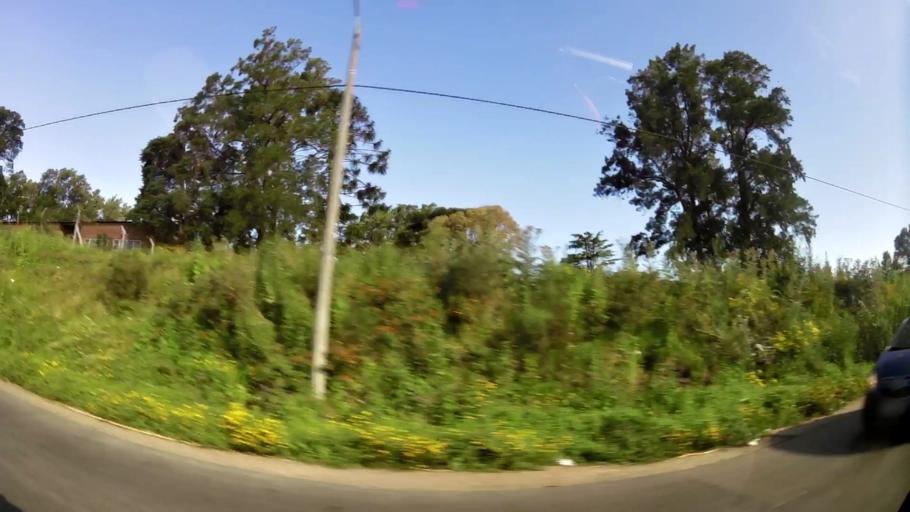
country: UY
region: Canelones
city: La Paz
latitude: -34.8206
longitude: -56.1764
